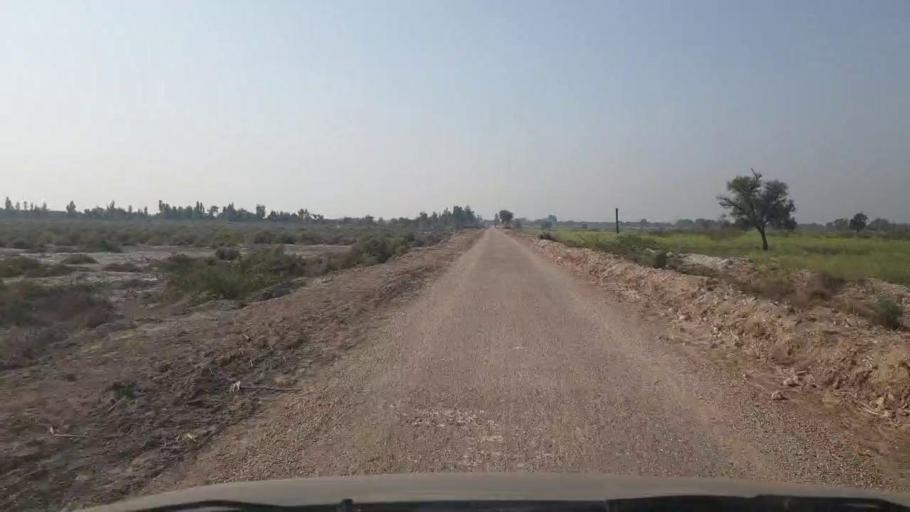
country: PK
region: Sindh
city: Mirwah Gorchani
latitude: 25.2649
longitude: 69.1150
